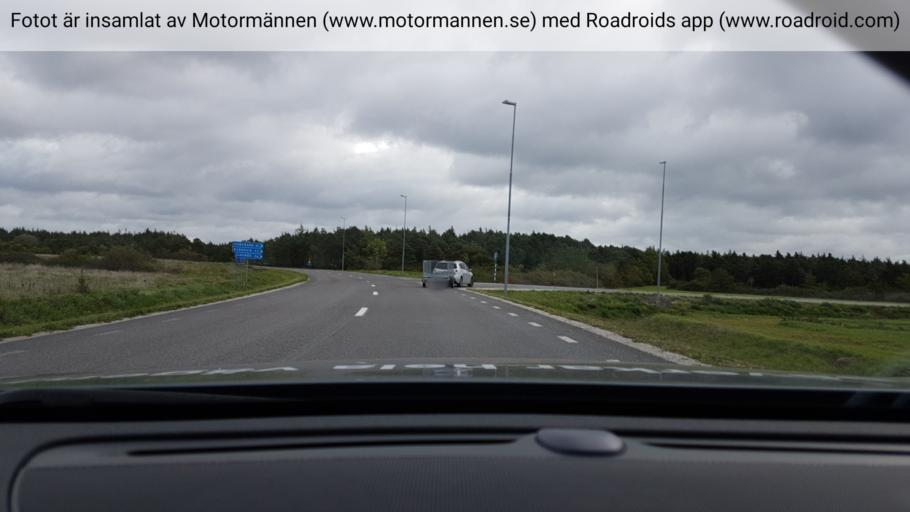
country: SE
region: Gotland
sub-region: Gotland
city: Klintehamn
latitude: 57.3806
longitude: 18.1983
